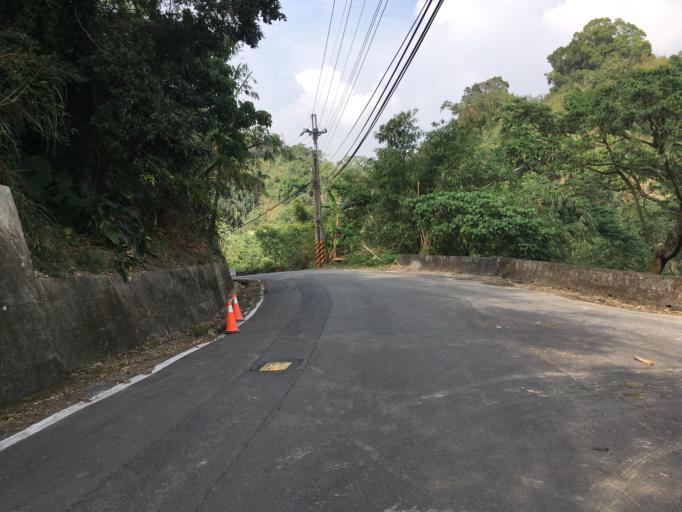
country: TW
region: Taiwan
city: Fengyuan
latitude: 24.1849
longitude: 120.7739
